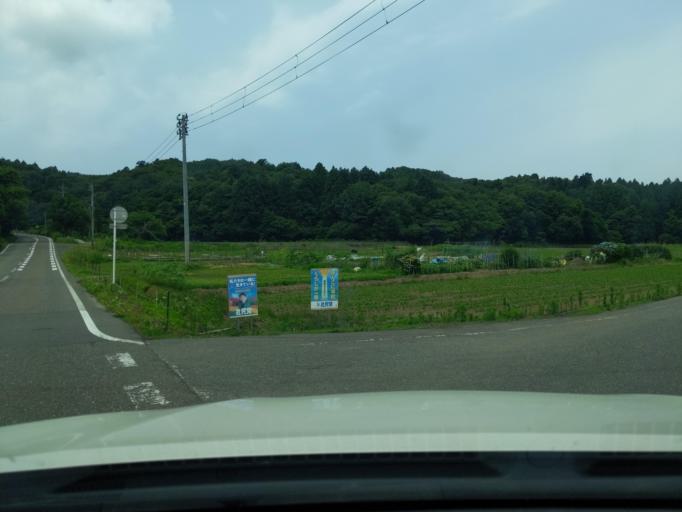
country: JP
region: Niigata
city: Kashiwazaki
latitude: 37.3328
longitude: 138.5566
